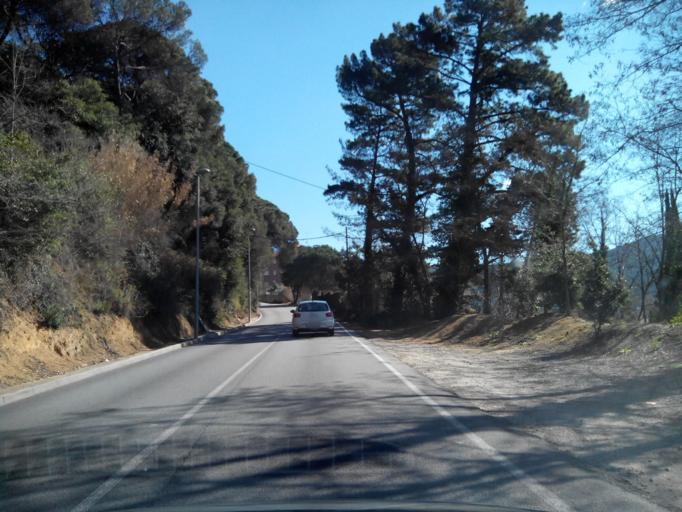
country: ES
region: Catalonia
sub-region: Provincia de Barcelona
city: Dosrius
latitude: 41.5976
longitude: 2.4013
